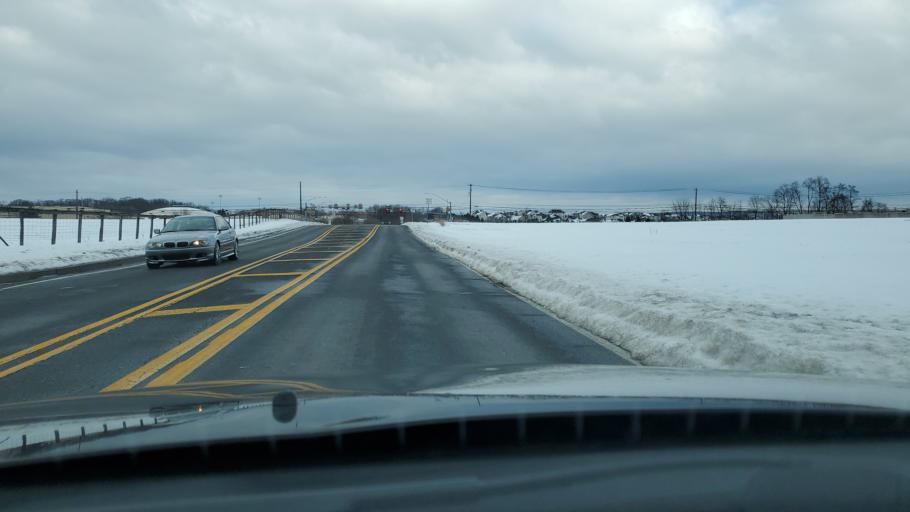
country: US
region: Pennsylvania
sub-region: Cumberland County
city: Mechanicsburg
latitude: 40.2366
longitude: -77.0582
